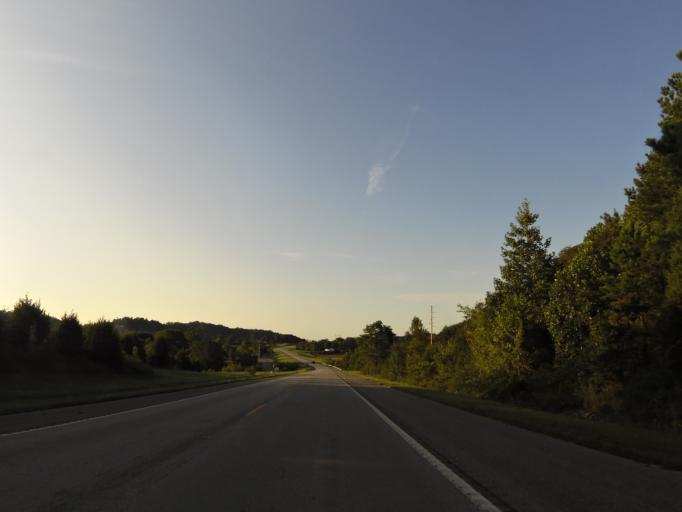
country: US
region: Tennessee
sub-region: Meigs County
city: Decatur
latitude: 35.5894
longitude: -84.6771
